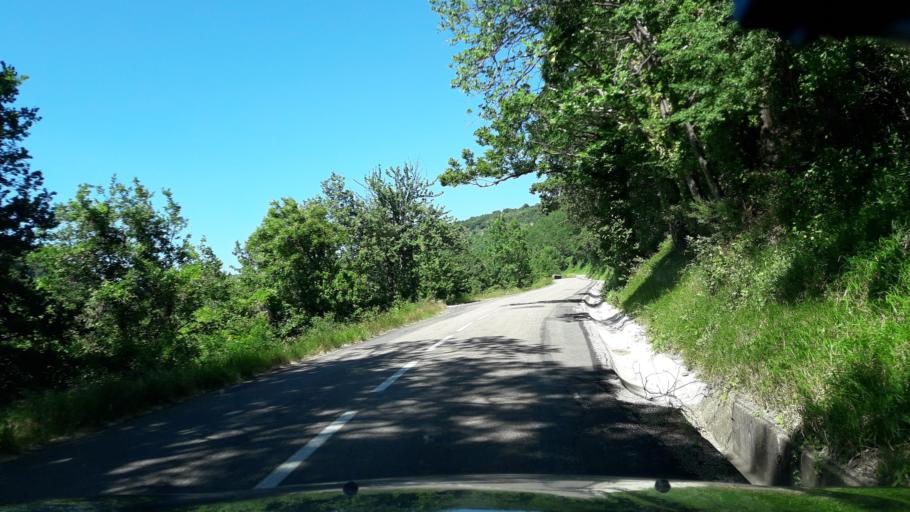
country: FR
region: Rhone-Alpes
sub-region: Departement de l'Ardeche
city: Villeneuve-de-Berg
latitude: 44.6252
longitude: 4.5426
